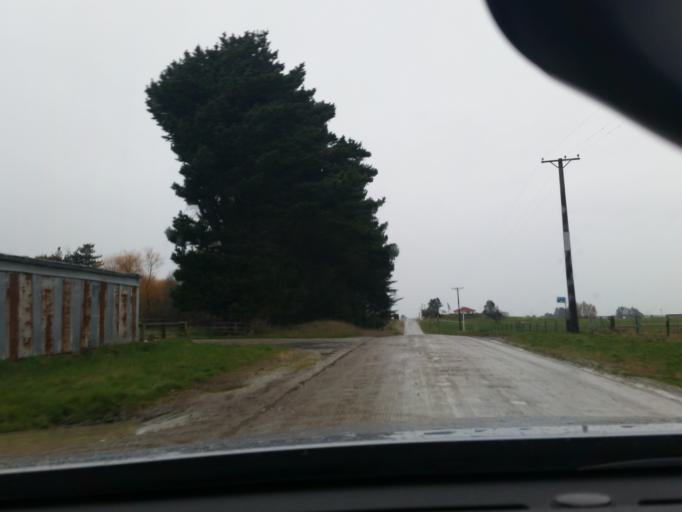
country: NZ
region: Southland
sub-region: Invercargill City
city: Invercargill
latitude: -46.4173
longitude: 168.5061
